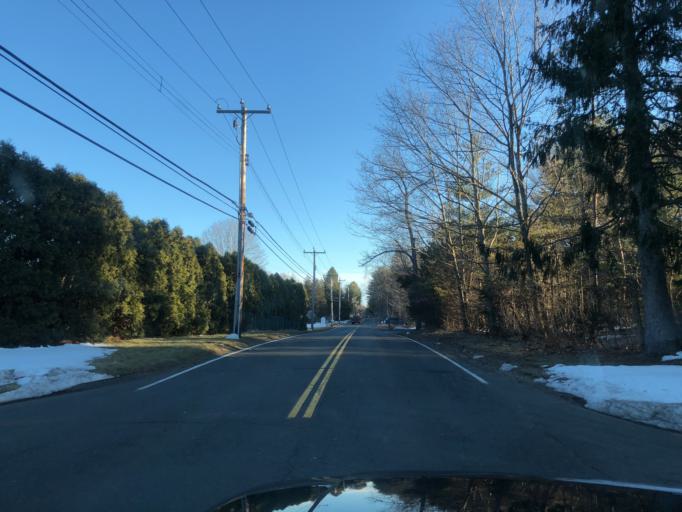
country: US
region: Connecticut
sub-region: Hartford County
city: Farmington
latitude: 41.7660
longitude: -72.8588
